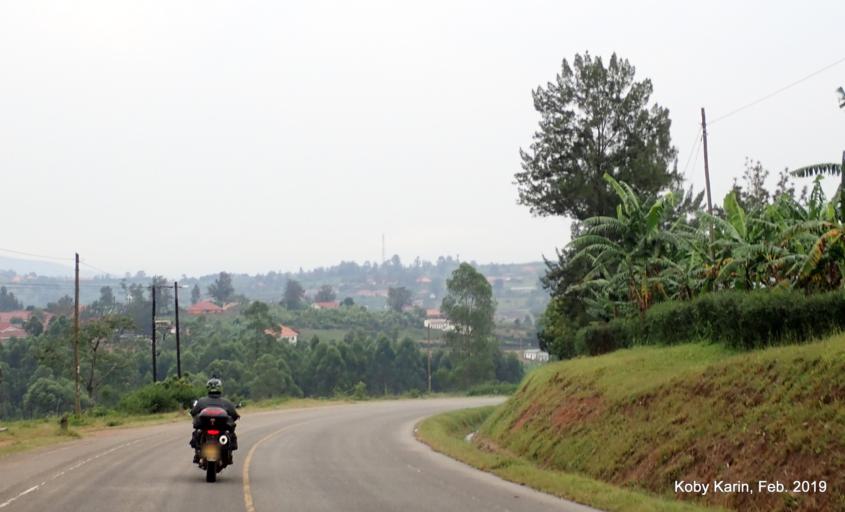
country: UG
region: Western Region
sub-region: Ntungamo District
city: Ntungamo
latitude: -0.8798
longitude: 30.2568
